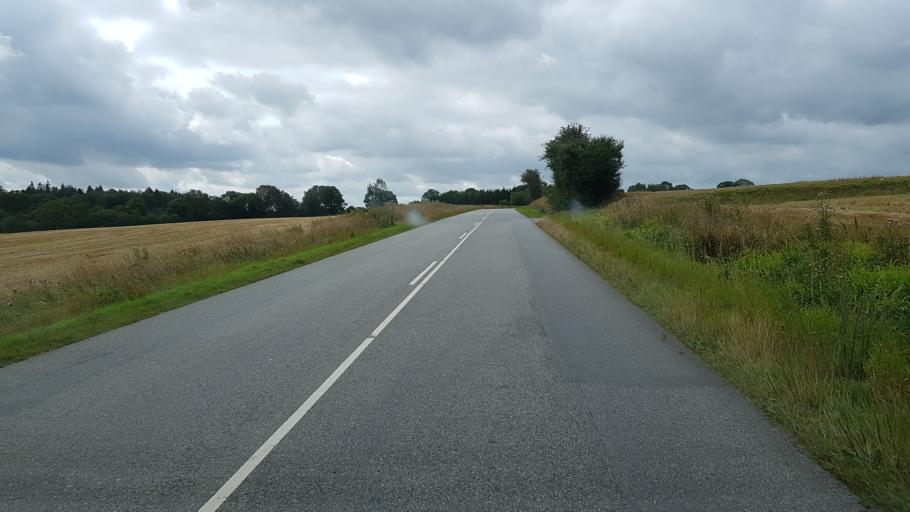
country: DK
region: South Denmark
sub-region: Kolding Kommune
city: Kolding
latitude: 55.4735
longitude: 9.4025
